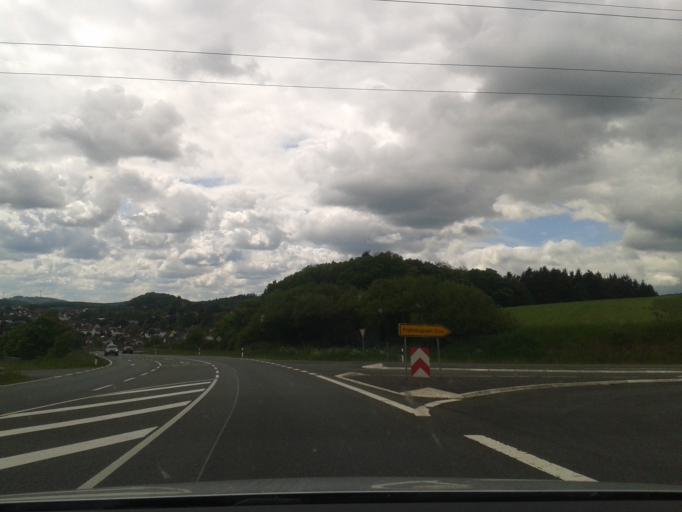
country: DE
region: Hesse
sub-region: Regierungsbezirk Giessen
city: Gladenbach
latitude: 50.7745
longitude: 8.5980
